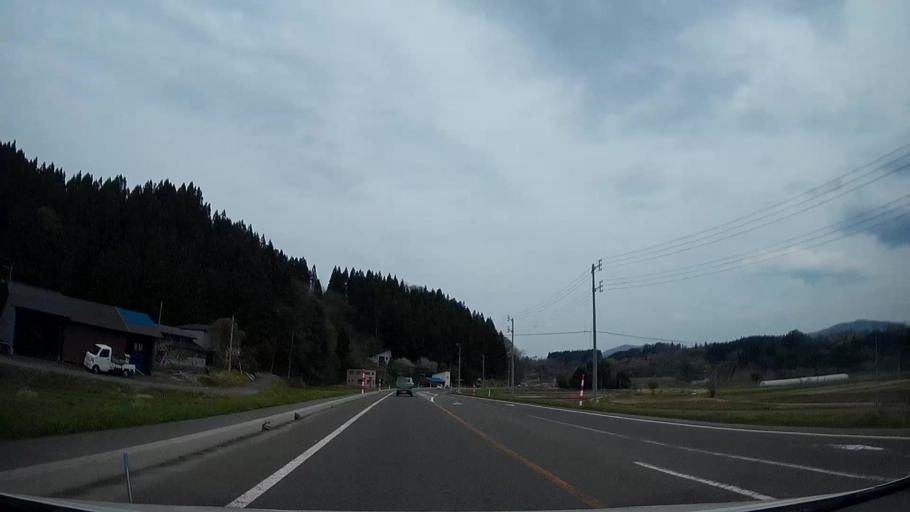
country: JP
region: Akita
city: Hanawa
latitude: 40.2744
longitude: 140.7934
